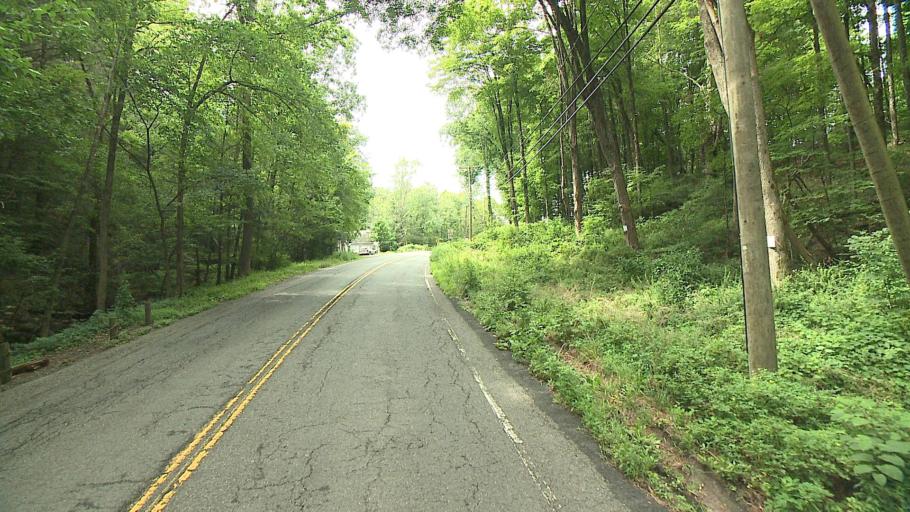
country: US
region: Connecticut
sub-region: Fairfield County
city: Sherman
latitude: 41.6395
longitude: -73.4966
